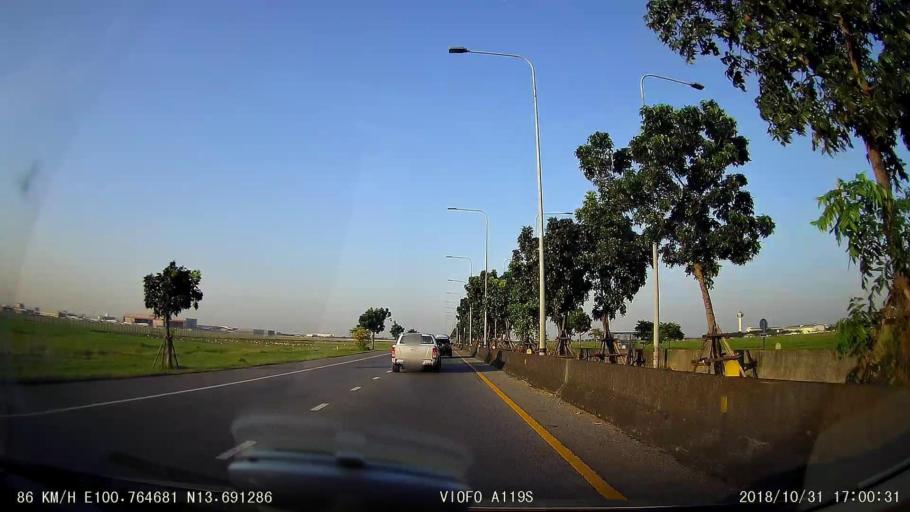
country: TH
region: Bangkok
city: Lat Krabang
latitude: 13.6915
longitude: 100.7648
